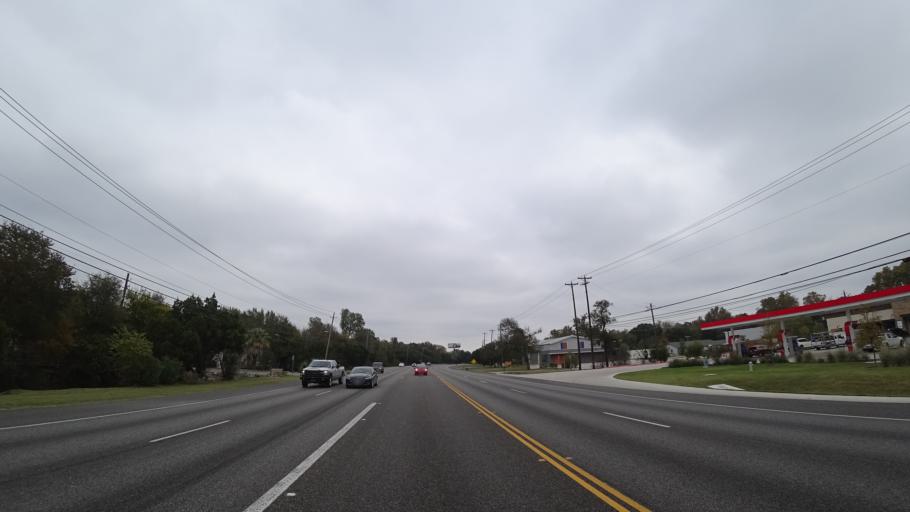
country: US
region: Texas
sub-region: Travis County
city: Barton Creek
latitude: 30.2468
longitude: -97.8881
